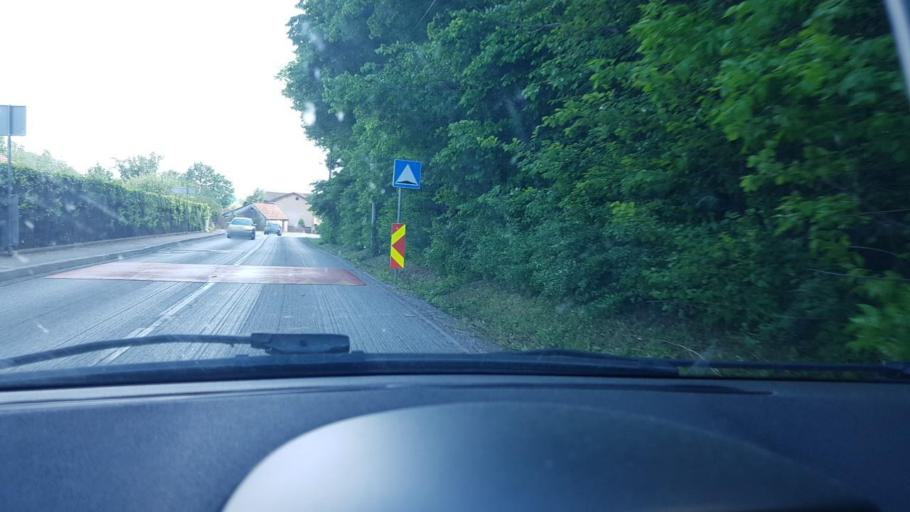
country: HR
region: Grad Zagreb
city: Dubrava
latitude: 45.8454
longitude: 16.0283
